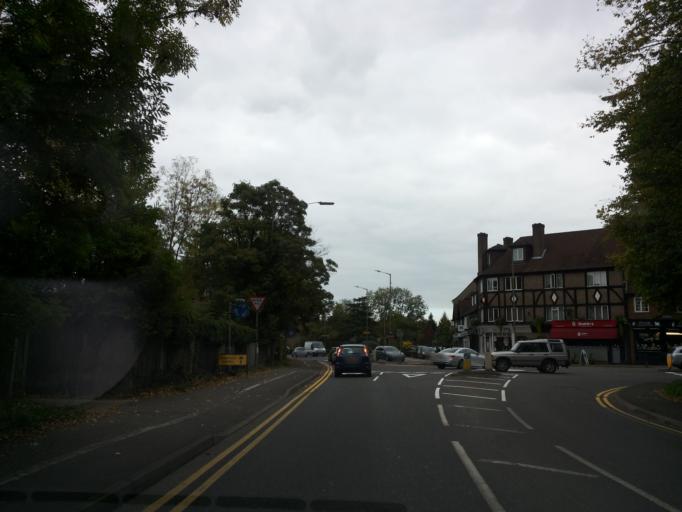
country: GB
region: England
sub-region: Buckinghamshire
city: Little Chalfont
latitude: 51.6673
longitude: -0.5663
